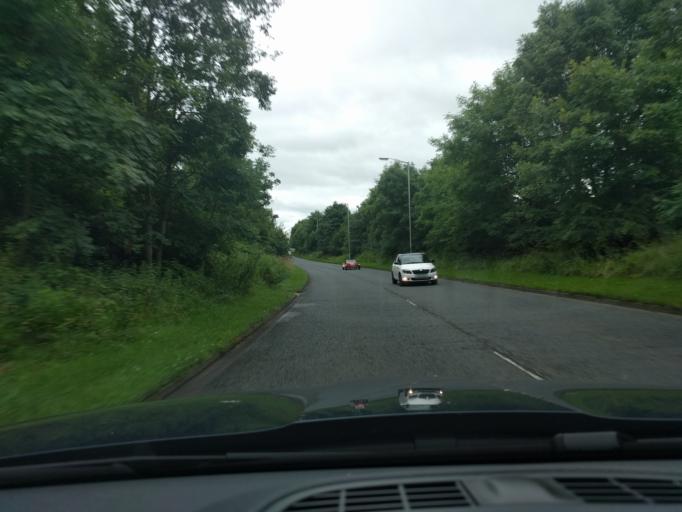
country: GB
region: England
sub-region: Northumberland
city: Cramlington
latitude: 55.0923
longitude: -1.5971
